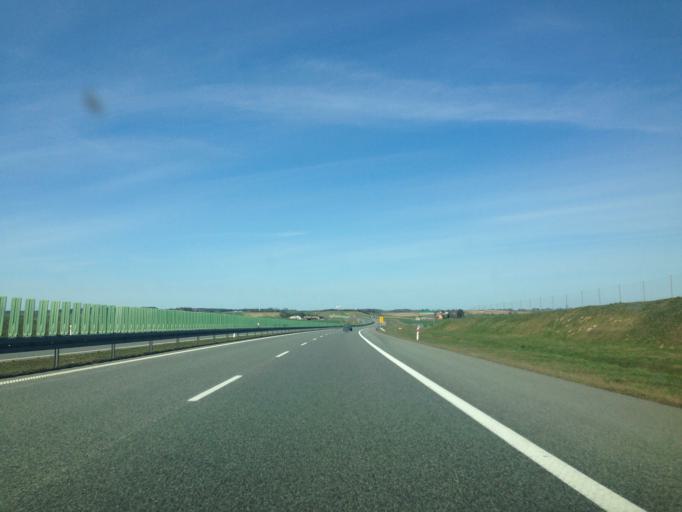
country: PL
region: Pomeranian Voivodeship
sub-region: Powiat starogardzki
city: Bobowo
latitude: 53.8508
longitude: 18.6271
